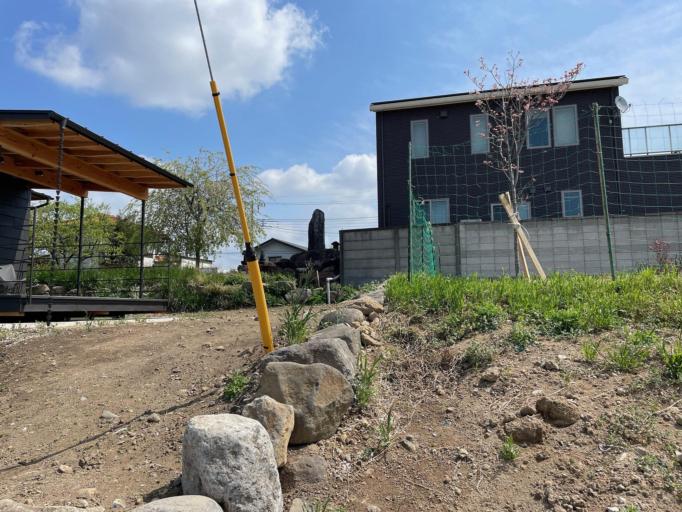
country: JP
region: Gunma
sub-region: Sawa-gun
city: Tamamura
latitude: 36.3047
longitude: 139.0862
